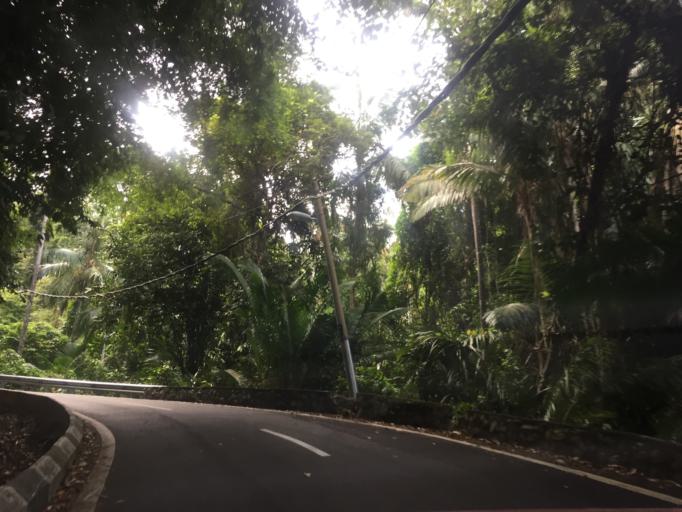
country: MY
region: Perak
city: Lumut
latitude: 4.2460
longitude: 100.5614
